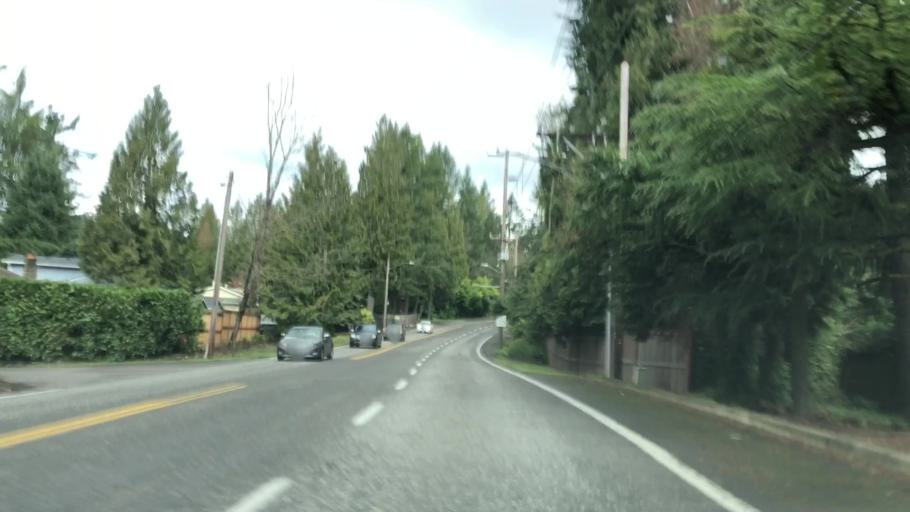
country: US
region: Oregon
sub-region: Washington County
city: West Slope
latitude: 45.4933
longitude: -122.7435
